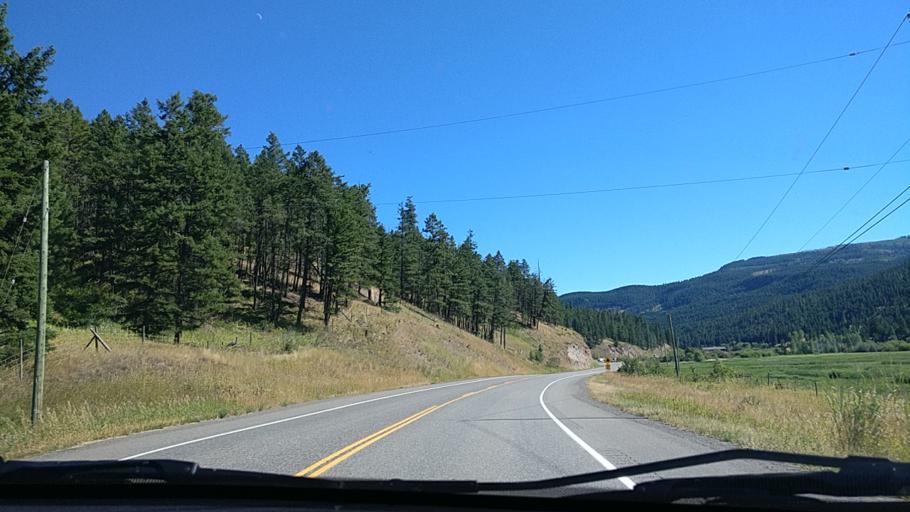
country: CA
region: British Columbia
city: Chase
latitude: 50.5734
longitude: -119.8865
